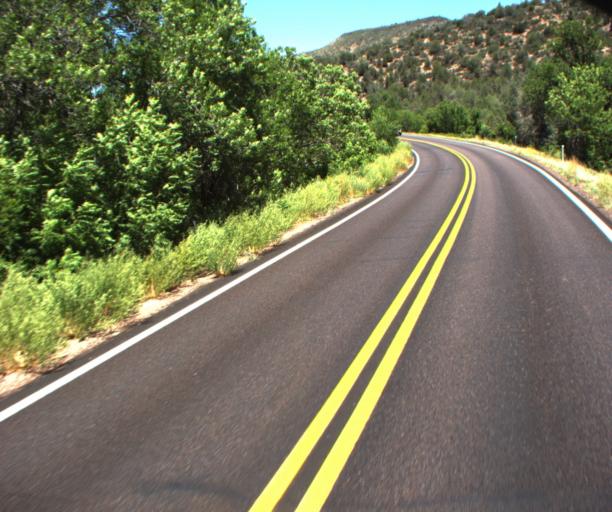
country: US
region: Arizona
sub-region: Gila County
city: Payson
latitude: 34.3077
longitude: -111.3613
